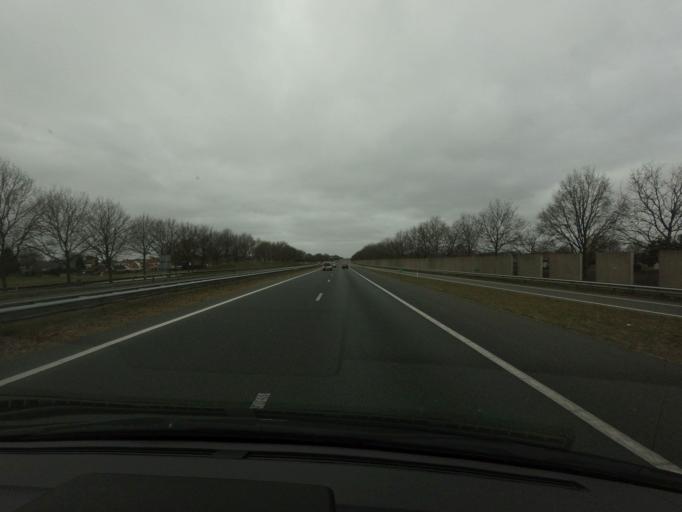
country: NL
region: Groningen
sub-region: Gemeente Hoogezand-Sappemeer
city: Sappemeer
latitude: 53.1679
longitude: 6.8028
